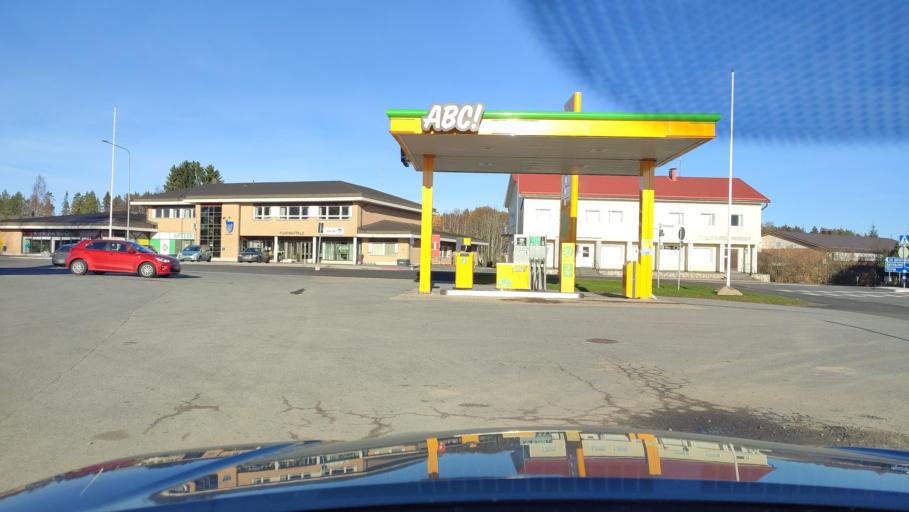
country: FI
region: Southern Ostrobothnia
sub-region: Suupohja
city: Karijoki
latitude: 62.3073
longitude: 21.7065
